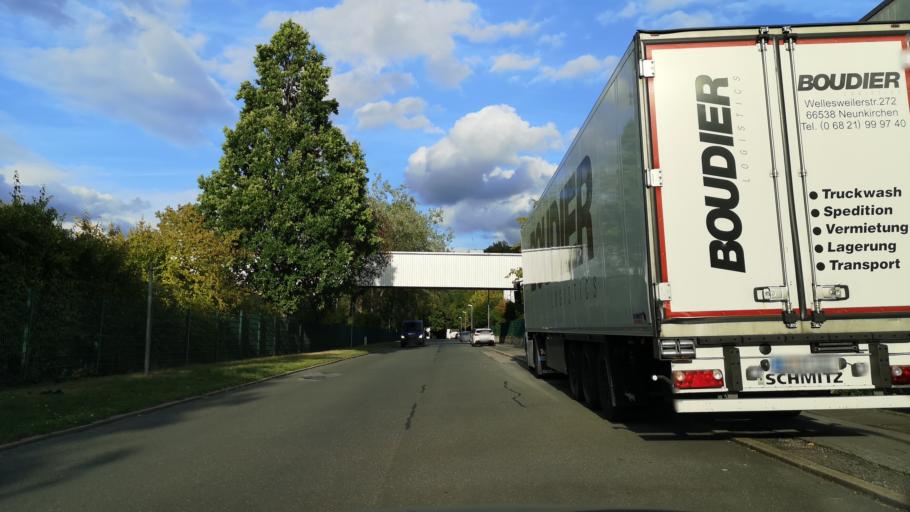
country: DE
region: North Rhine-Westphalia
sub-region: Regierungsbezirk Dusseldorf
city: Velbert
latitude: 51.3792
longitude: 7.0947
